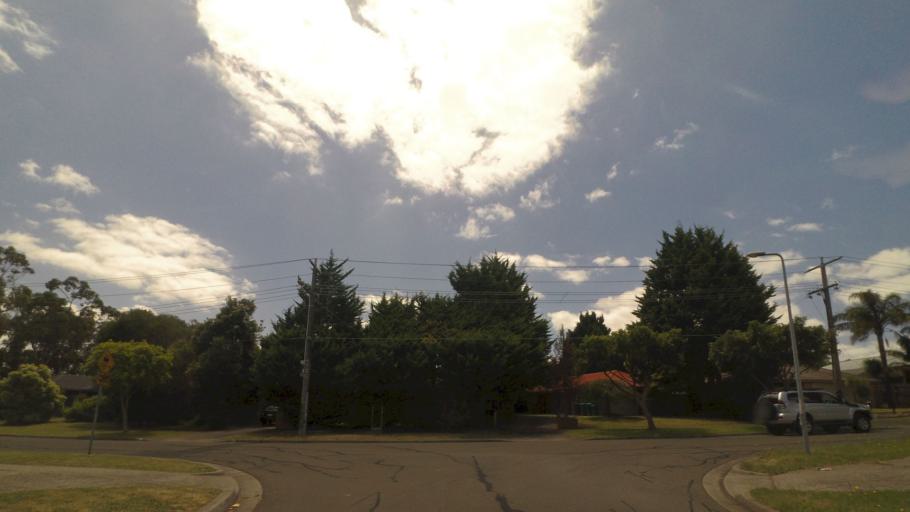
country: AU
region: Victoria
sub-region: Maroondah
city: Bayswater North
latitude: -37.8244
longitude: 145.2967
